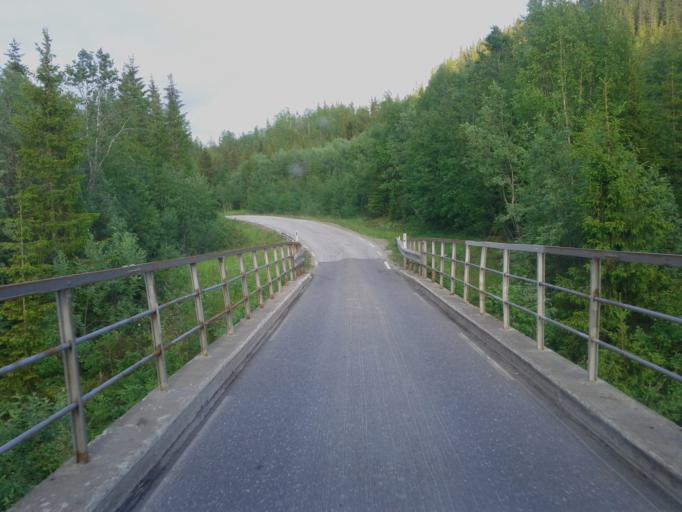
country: NO
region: Nordland
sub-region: Grane
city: Trofors
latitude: 65.5184
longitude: 13.6301
